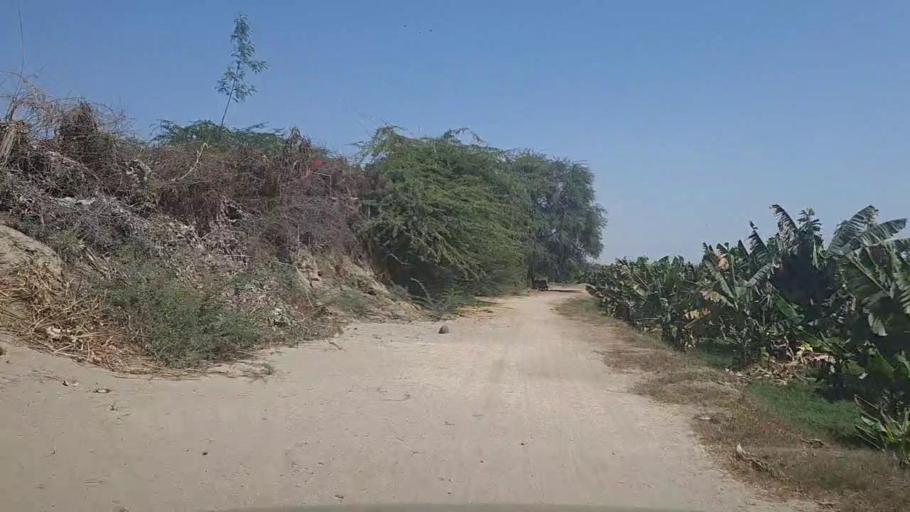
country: PK
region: Sindh
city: Thatta
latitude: 24.7911
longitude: 68.0149
